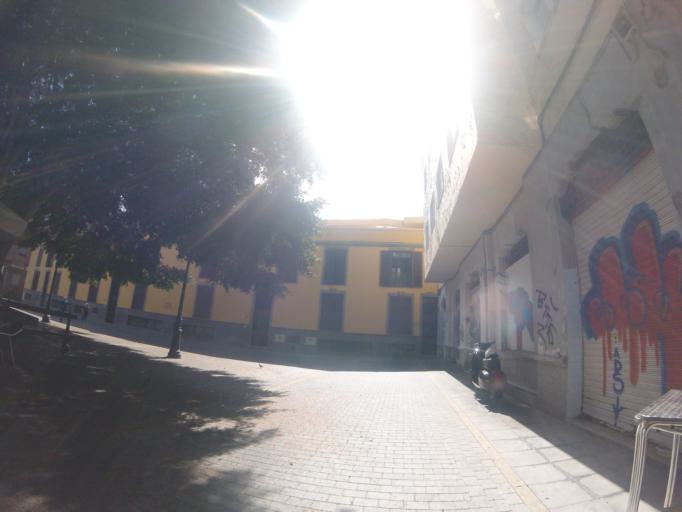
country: ES
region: Canary Islands
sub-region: Provincia de Santa Cruz de Tenerife
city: Santa Cruz de Tenerife
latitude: 28.4652
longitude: -16.2506
